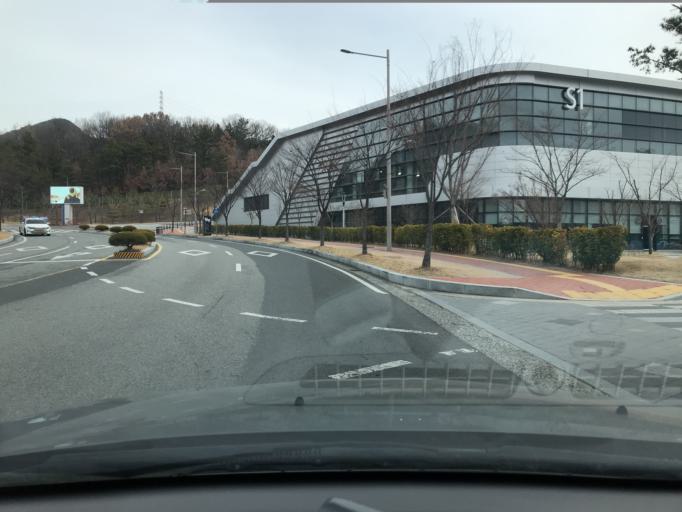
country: KR
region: Daegu
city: Hwawon
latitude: 35.7006
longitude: 128.4584
